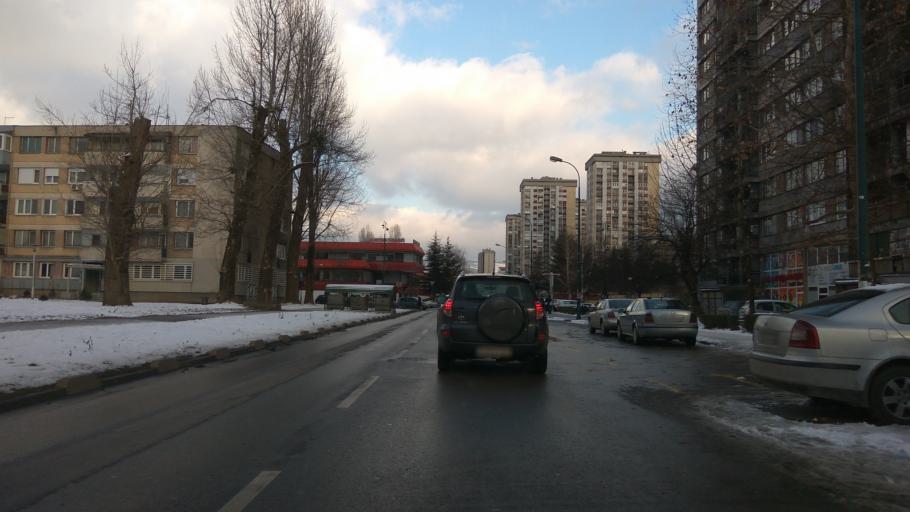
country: BA
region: Federation of Bosnia and Herzegovina
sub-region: Kanton Sarajevo
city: Sarajevo
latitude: 43.8536
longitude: 18.3838
